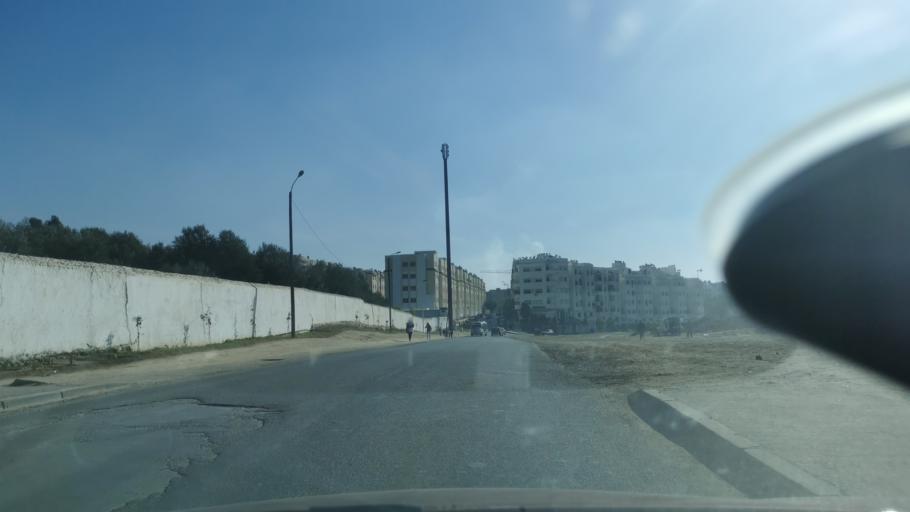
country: MA
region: Fes-Boulemane
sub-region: Fes
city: Fes
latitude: 34.0399
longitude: -4.9897
